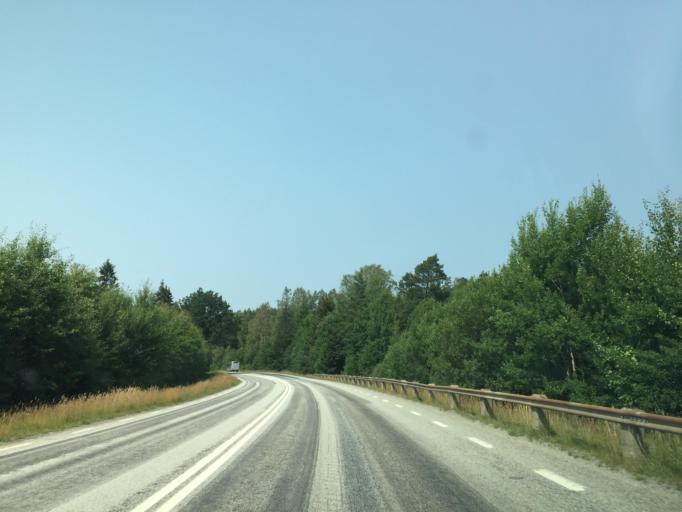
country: SE
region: Vaestra Goetaland
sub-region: Uddevalla Kommun
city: Ljungskile
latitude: 58.1113
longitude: 11.9908
